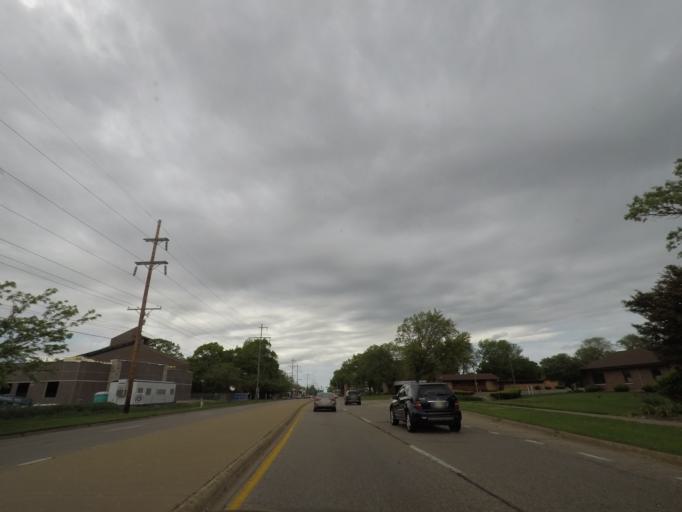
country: US
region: Illinois
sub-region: Winnebago County
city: Loves Park
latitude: 42.2834
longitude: -89.0290
